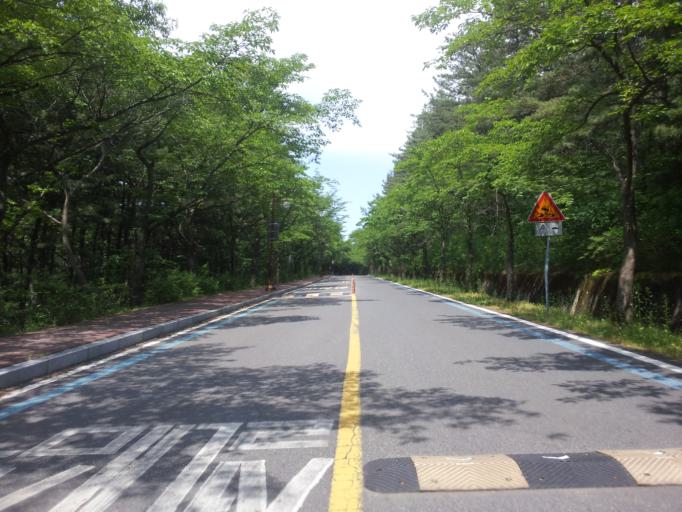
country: KR
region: Daejeon
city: Sintansin
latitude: 36.4730
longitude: 127.4769
